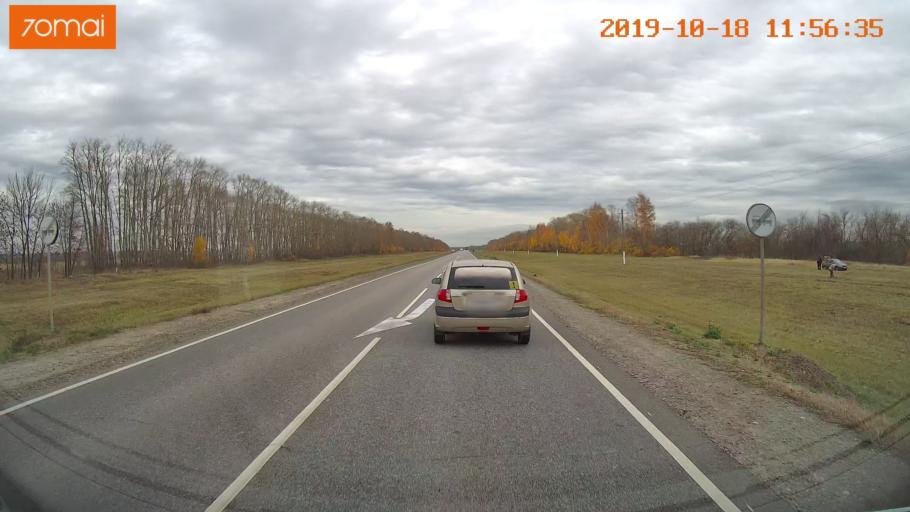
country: RU
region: Rjazan
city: Mikhaylov
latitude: 54.2657
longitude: 39.1219
